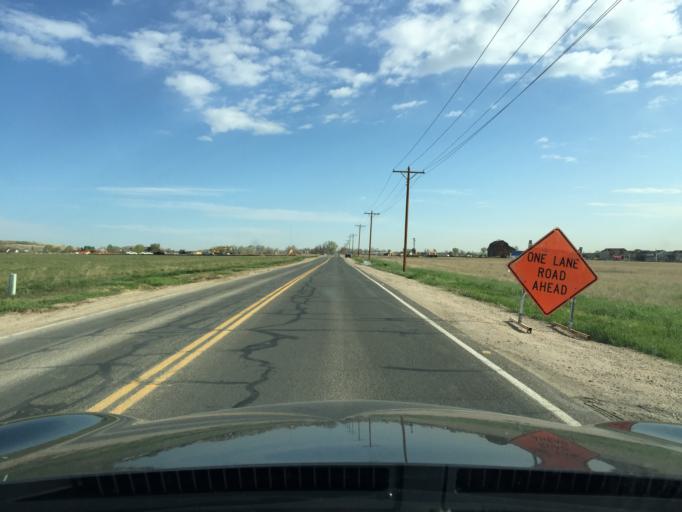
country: US
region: Colorado
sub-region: Boulder County
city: Erie
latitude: 40.0012
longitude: -104.9991
